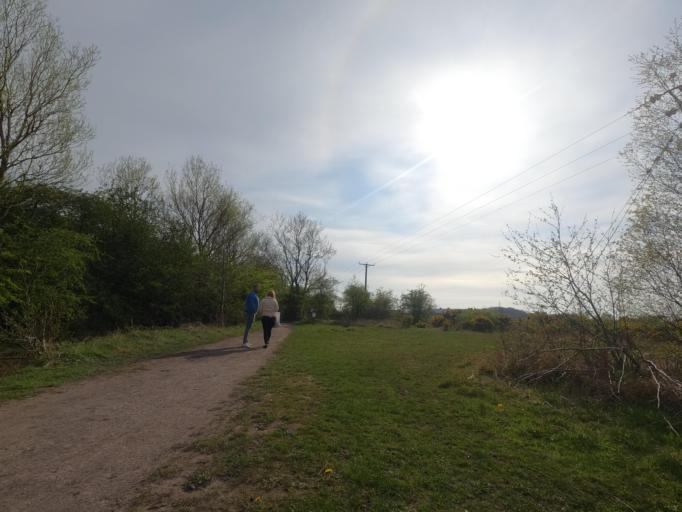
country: GB
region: England
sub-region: Newcastle upon Tyne
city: Hazlerigg
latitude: 55.0371
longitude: -1.6499
